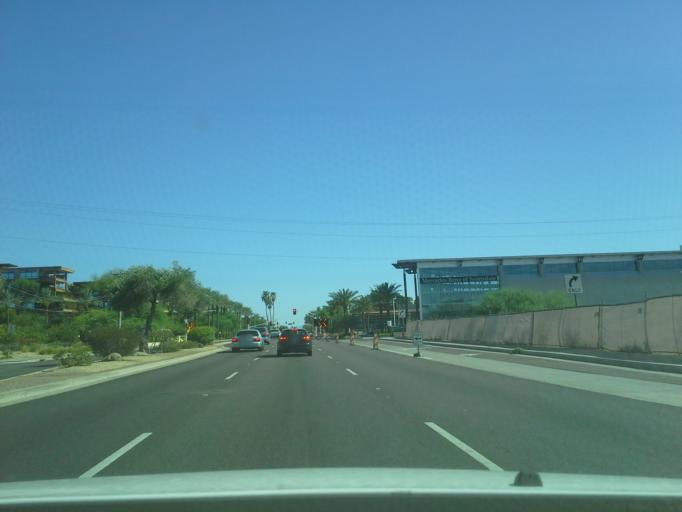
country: US
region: Arizona
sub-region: Maricopa County
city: Scottsdale
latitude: 33.5045
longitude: -111.9260
